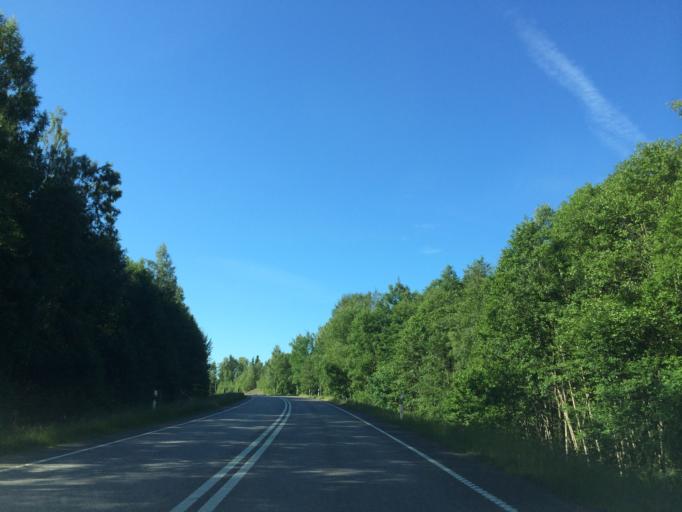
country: SE
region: OEstergoetland
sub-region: Motala Kommun
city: Ryd
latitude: 58.6491
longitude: 14.9553
